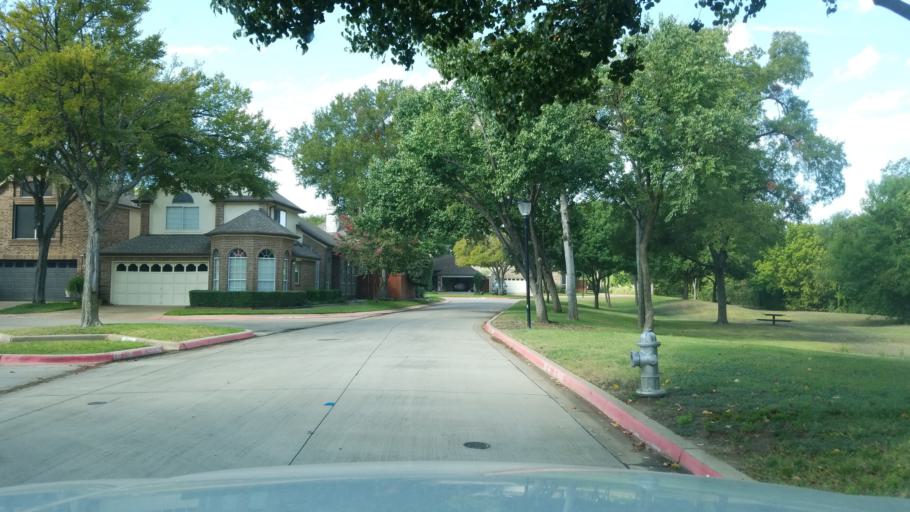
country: US
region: Texas
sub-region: Tarrant County
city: Euless
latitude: 32.8467
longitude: -97.0768
